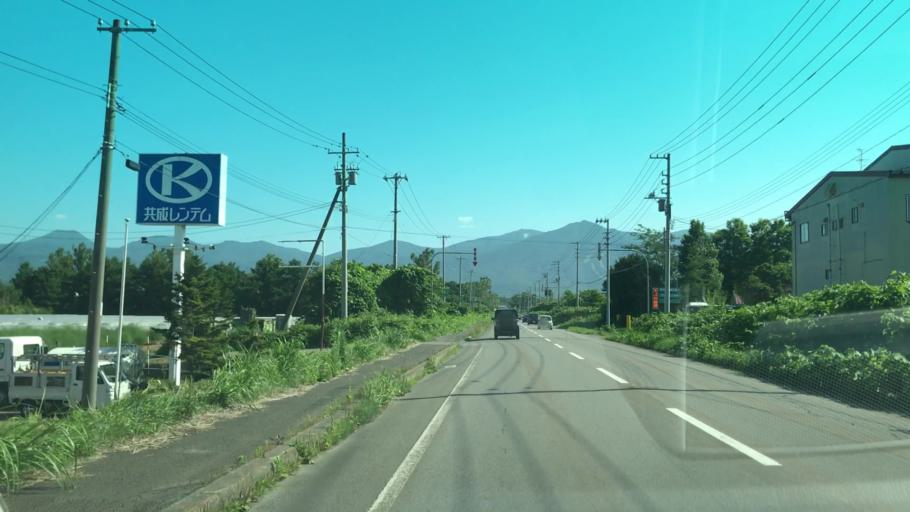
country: JP
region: Hokkaido
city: Iwanai
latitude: 43.0117
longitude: 140.5436
